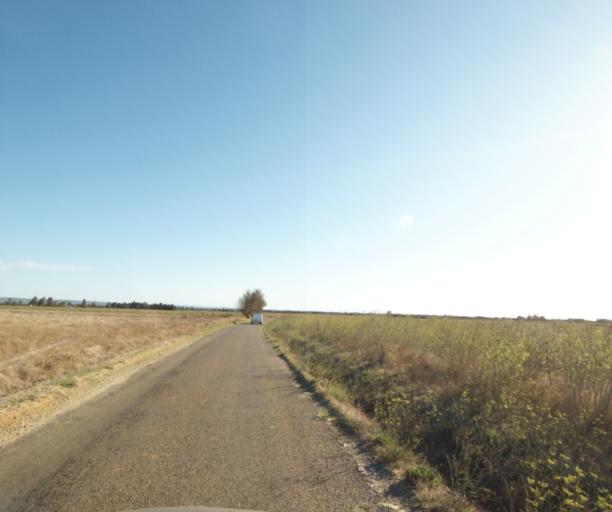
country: FR
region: Languedoc-Roussillon
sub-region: Departement du Gard
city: Bouillargues
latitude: 43.7970
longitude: 4.4434
